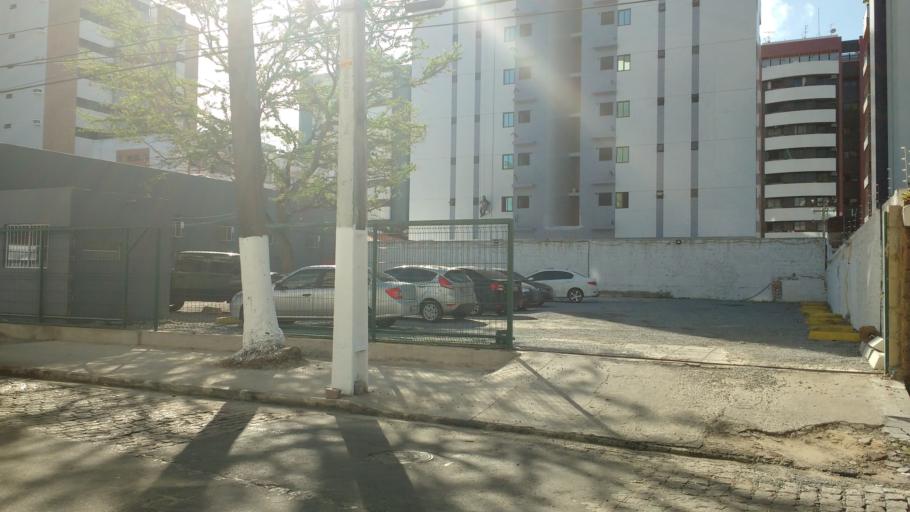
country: BR
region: Alagoas
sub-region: Maceio
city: Maceio
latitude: -9.6487
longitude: -35.7031
